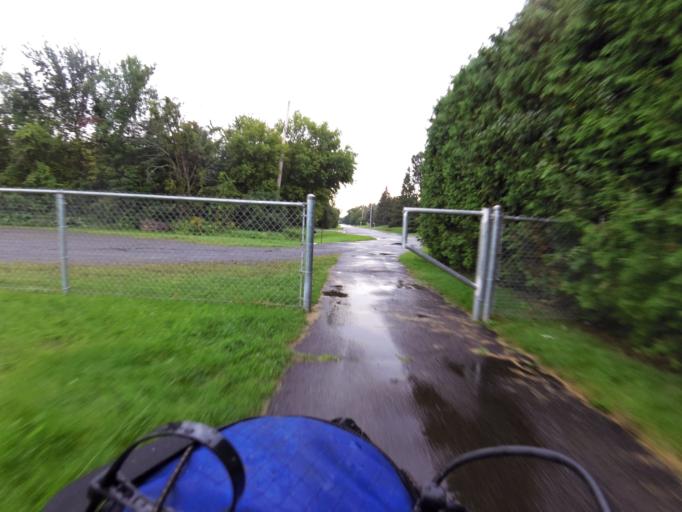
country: CA
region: Ontario
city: Ottawa
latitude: 45.2368
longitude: -75.4797
